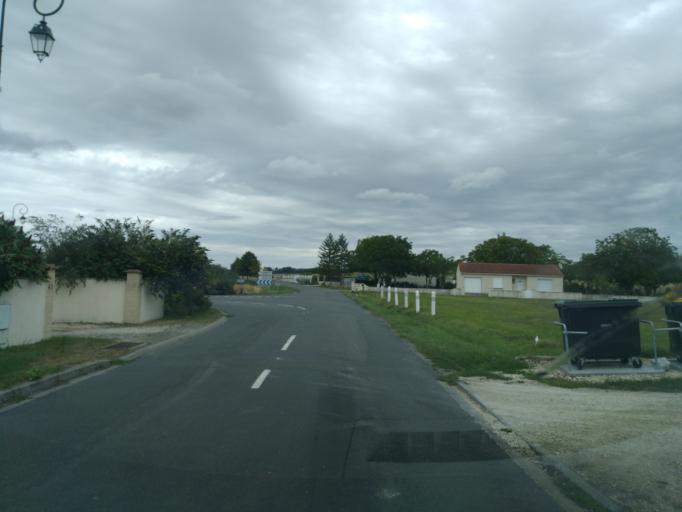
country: FR
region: Poitou-Charentes
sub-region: Departement de la Charente-Maritime
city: Pons
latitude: 45.5993
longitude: -0.5131
